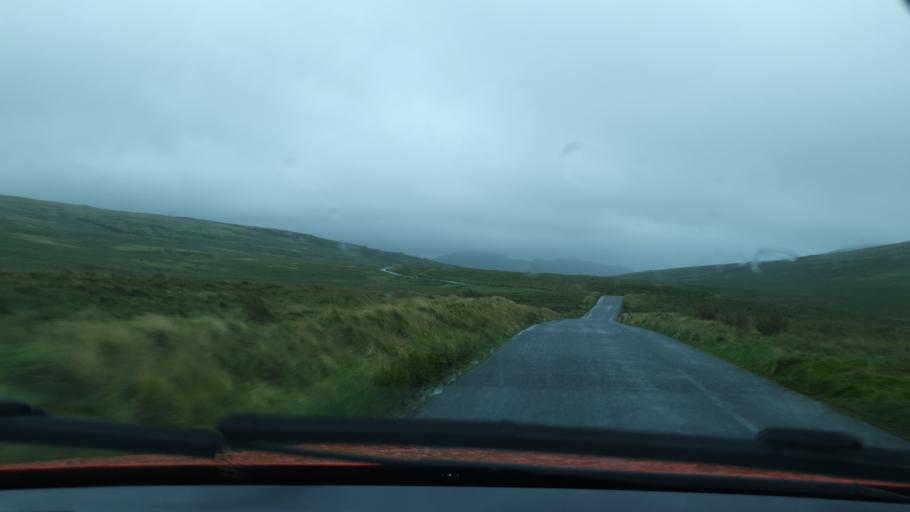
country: GB
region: England
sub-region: Cumbria
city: Millom
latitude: 54.3572
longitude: -3.2659
